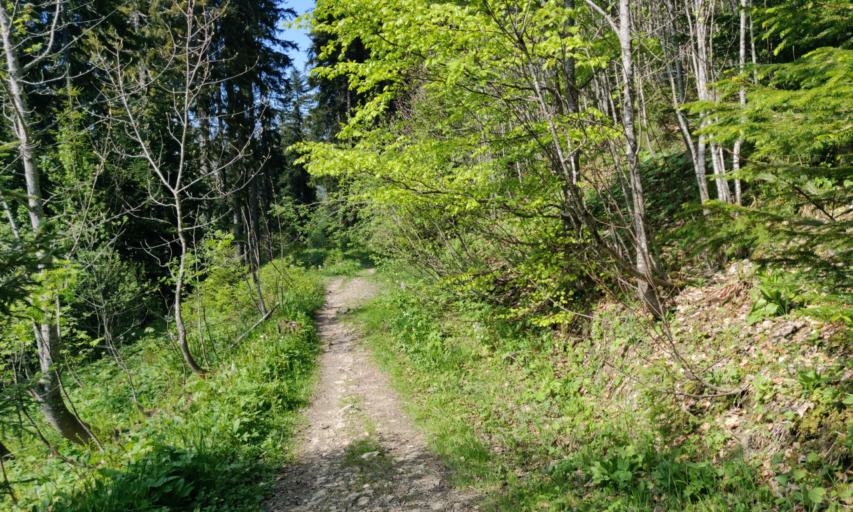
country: CH
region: Fribourg
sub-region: Gruyere District
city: Vuadens
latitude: 46.5575
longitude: 7.0205
